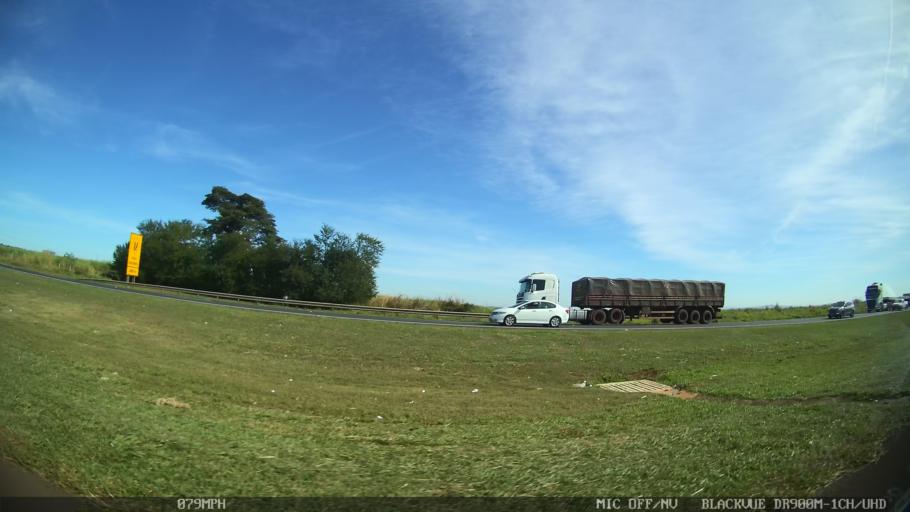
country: BR
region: Sao Paulo
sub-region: Araras
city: Araras
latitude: -22.4291
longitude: -47.3940
